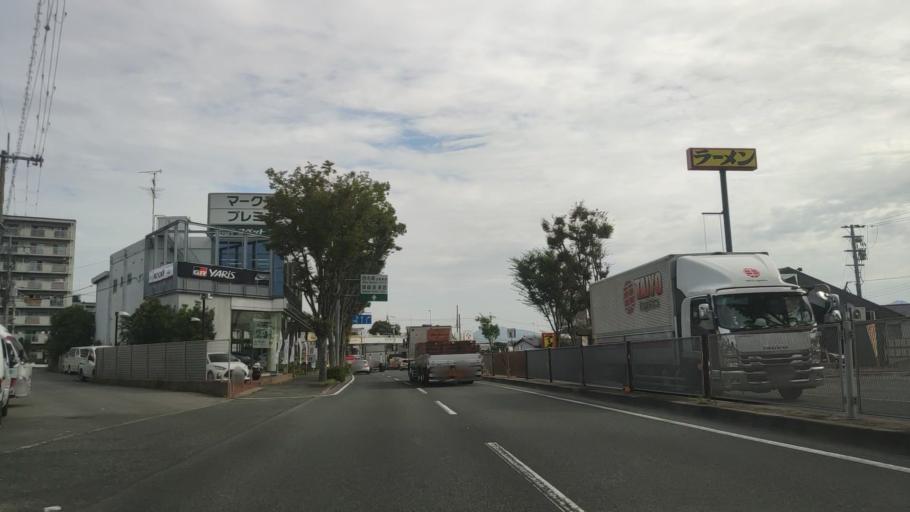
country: JP
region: Osaka
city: Tondabayashicho
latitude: 34.5076
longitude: 135.6000
